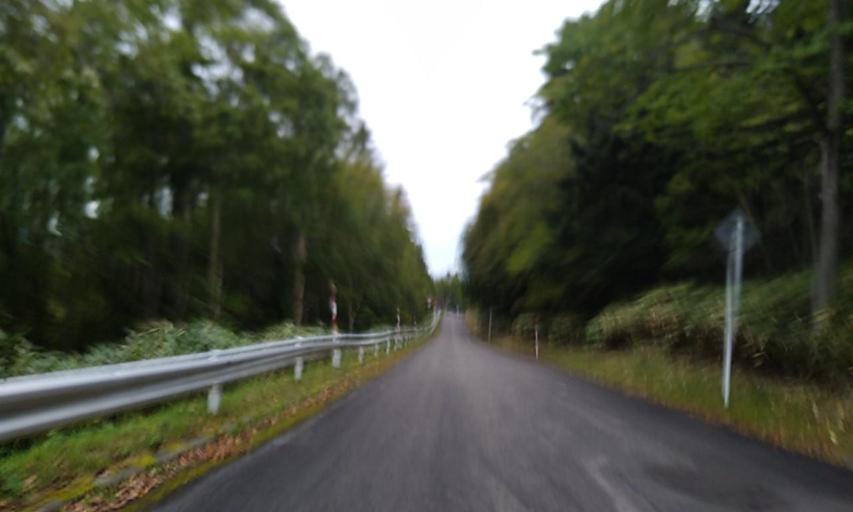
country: JP
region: Hokkaido
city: Bihoro
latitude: 43.5657
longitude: 144.2107
